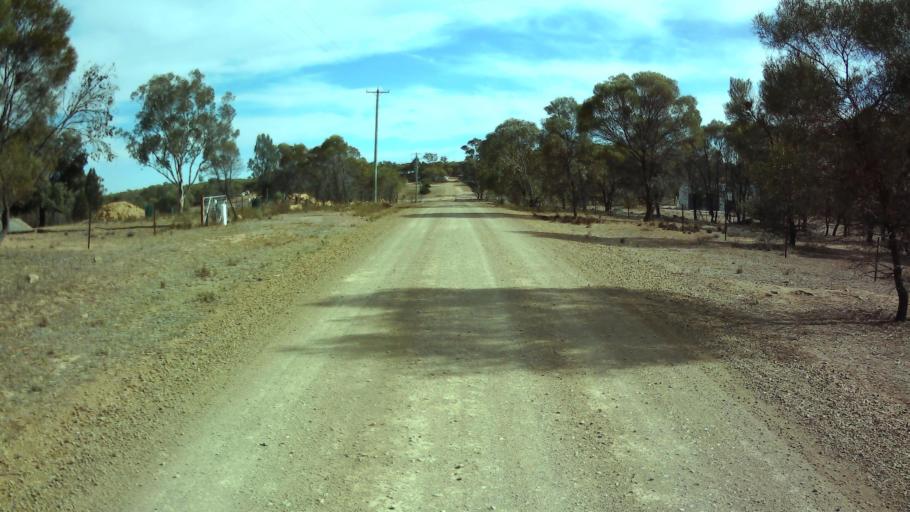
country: AU
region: New South Wales
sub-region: Weddin
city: Grenfell
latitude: -33.8717
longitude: 148.1922
